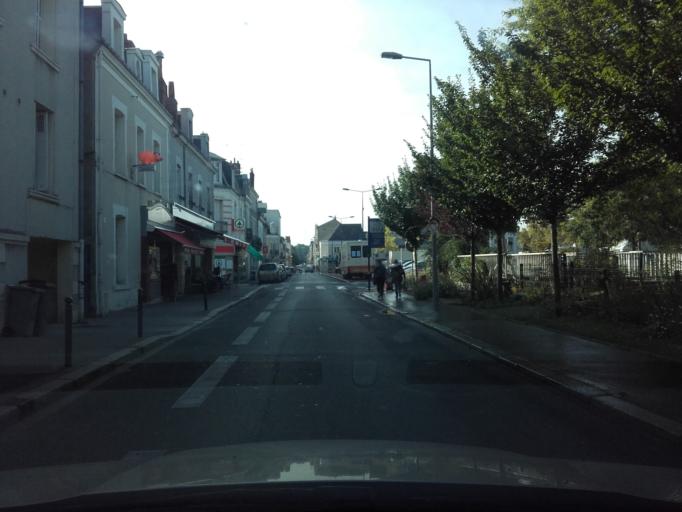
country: FR
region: Centre
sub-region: Departement d'Indre-et-Loire
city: Tours
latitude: 47.3881
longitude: 0.7030
